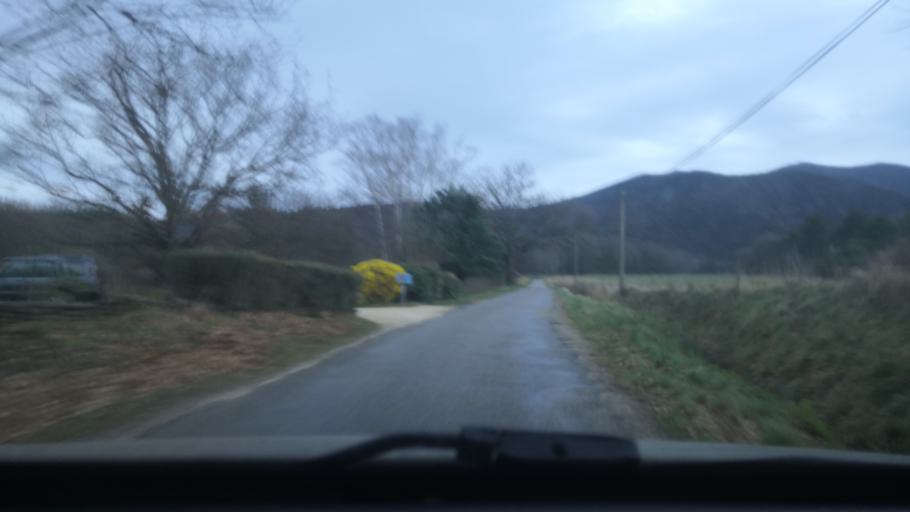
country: FR
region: Rhone-Alpes
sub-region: Departement de la Drome
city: Dieulefit
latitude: 44.5235
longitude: 5.0226
